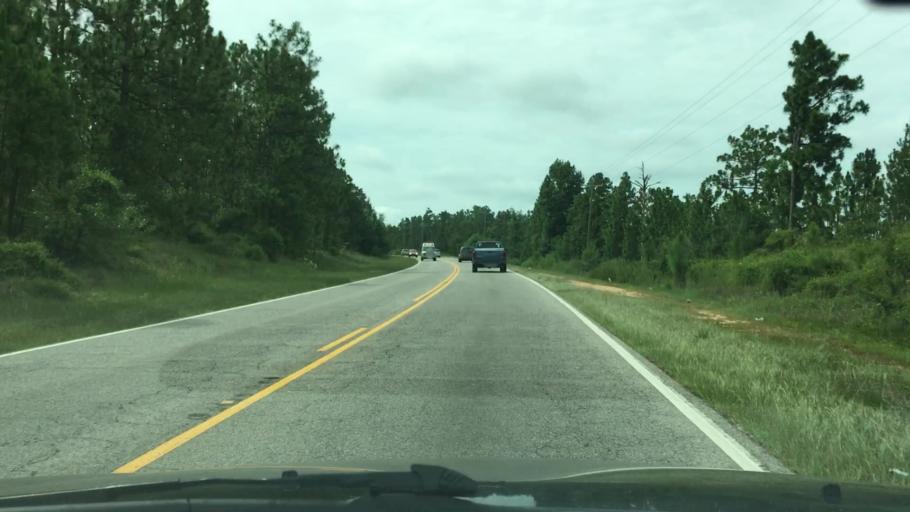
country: US
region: South Carolina
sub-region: Aiken County
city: Warrenville
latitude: 33.5376
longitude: -81.7747
